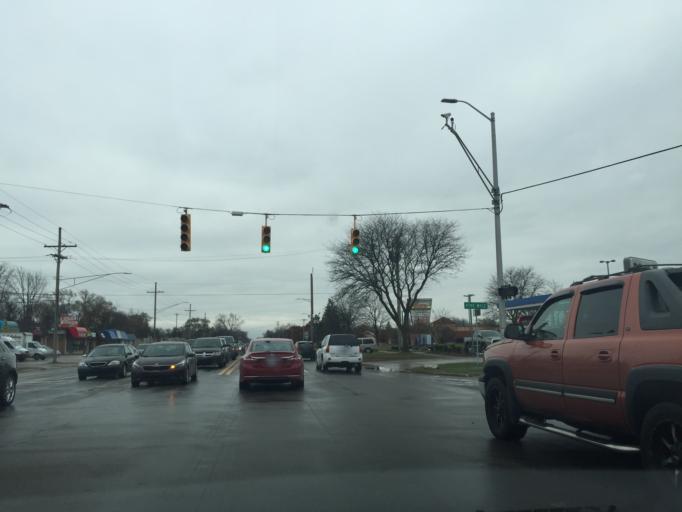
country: US
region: Michigan
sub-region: Wayne County
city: Livonia
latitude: 42.3983
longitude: -83.3346
